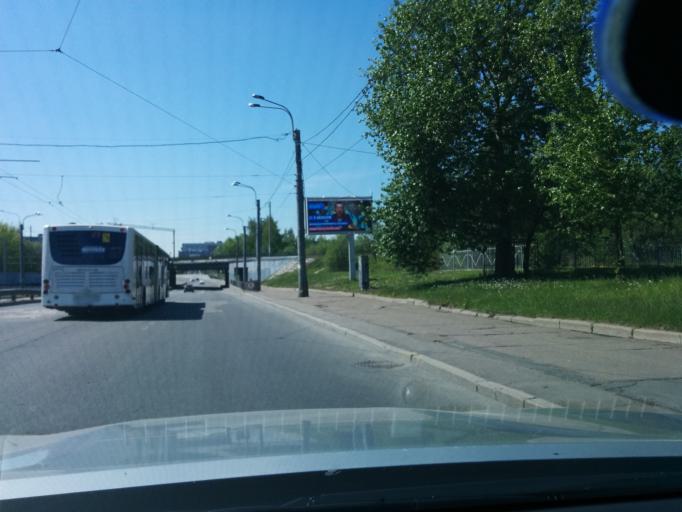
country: RU
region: St.-Petersburg
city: Krasnogvargeisky
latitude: 59.9378
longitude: 30.4501
